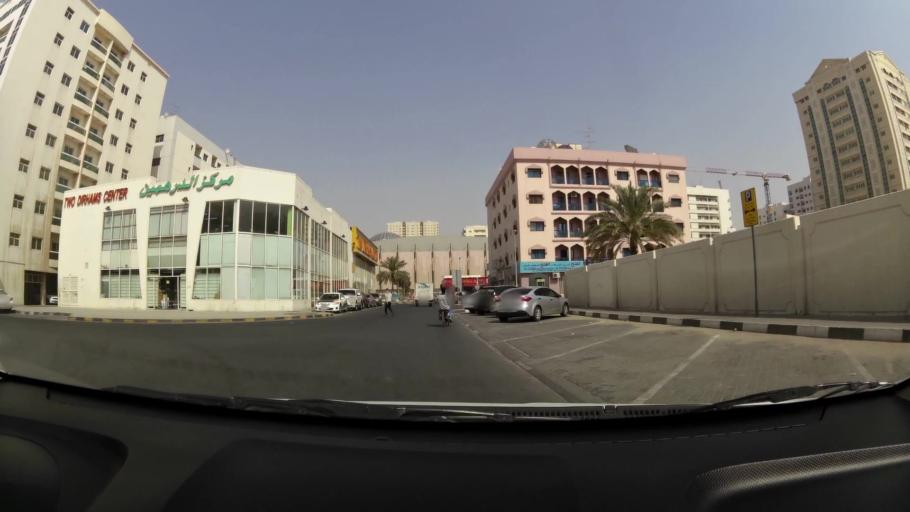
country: AE
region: Ash Shariqah
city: Sharjah
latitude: 25.3464
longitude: 55.3968
